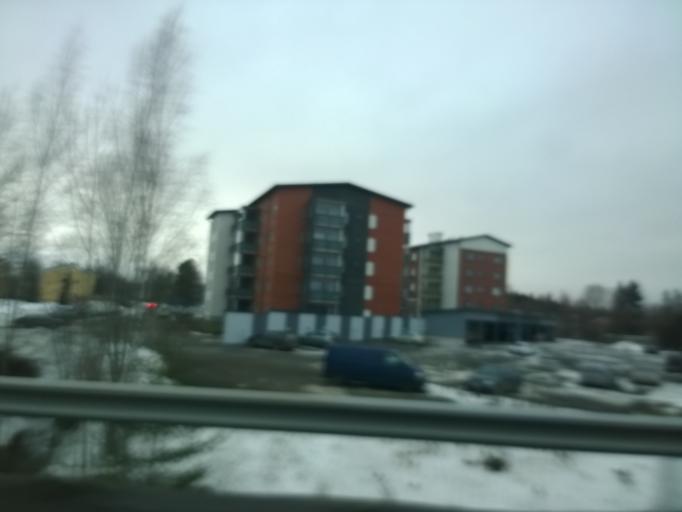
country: FI
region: Pirkanmaa
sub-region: Tampere
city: Lempaeaelae
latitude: 61.3058
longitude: 23.7565
